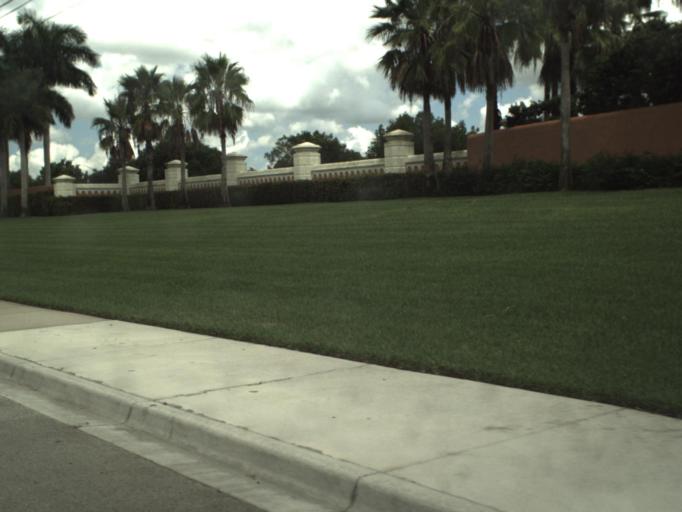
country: US
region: Florida
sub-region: Palm Beach County
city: Wellington
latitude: 26.6509
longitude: -80.1859
